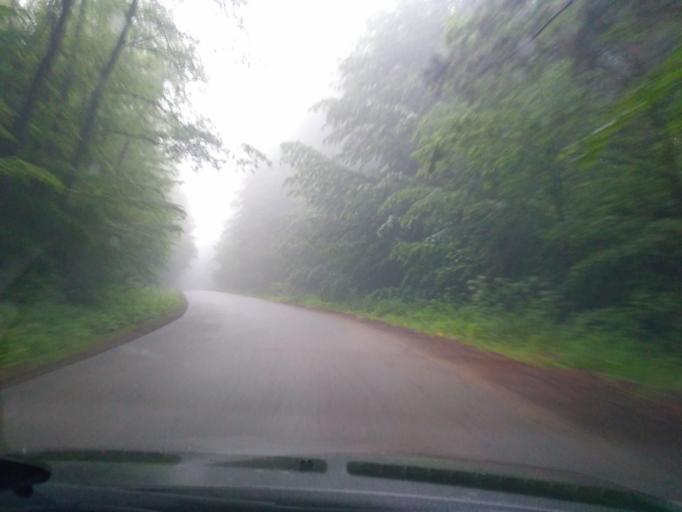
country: PL
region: Subcarpathian Voivodeship
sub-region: Powiat debicki
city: Debica
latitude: 49.9724
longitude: 21.3968
